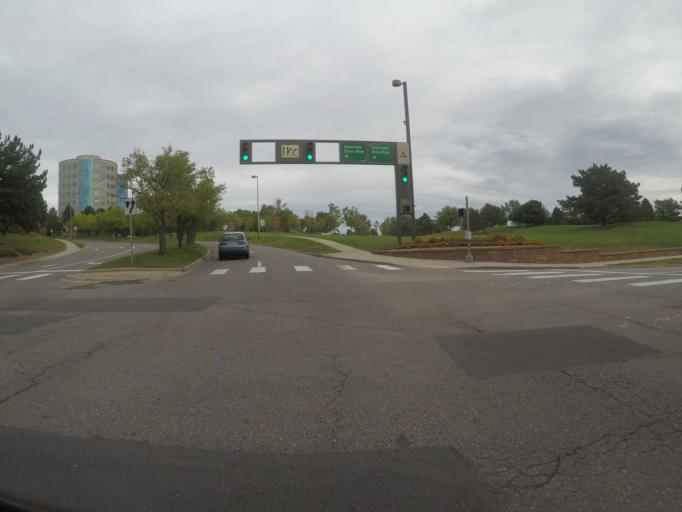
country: US
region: Colorado
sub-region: Arapahoe County
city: Centennial
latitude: 39.5667
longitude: -104.8668
